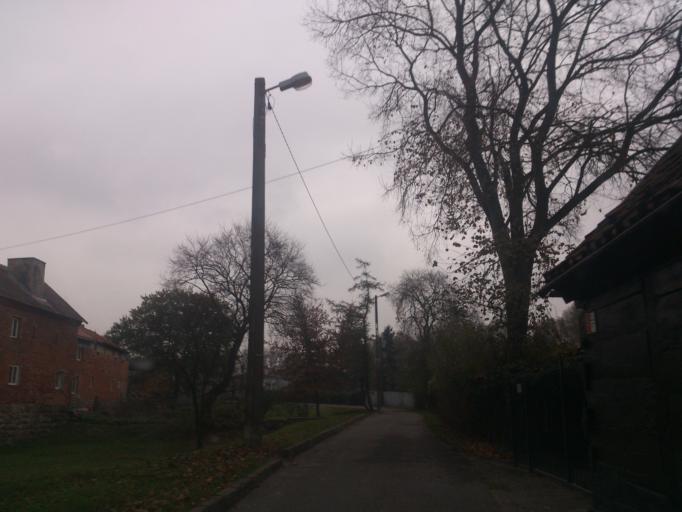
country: PL
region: Kujawsko-Pomorskie
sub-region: Powiat golubsko-dobrzynski
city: Golub-Dobrzyn
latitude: 53.1122
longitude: 19.0536
